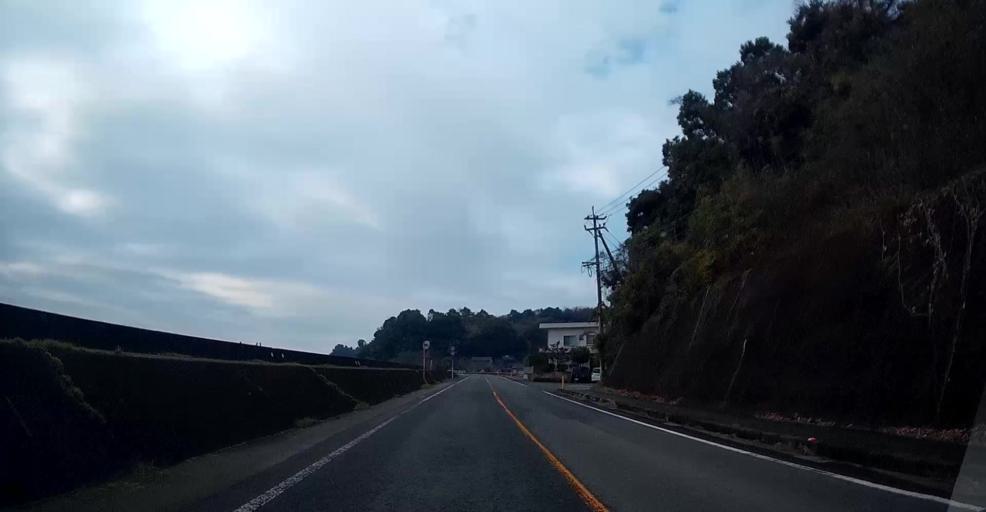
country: JP
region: Kumamoto
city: Matsubase
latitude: 32.6386
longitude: 130.6415
